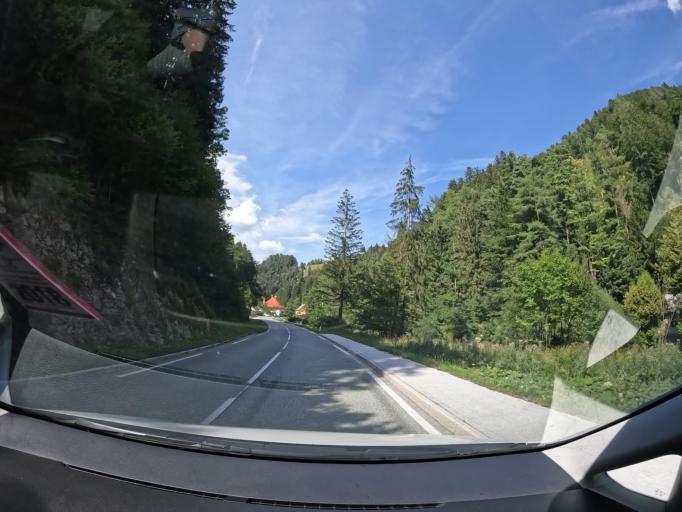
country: SI
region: Preddvor
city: Preddvor
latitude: 46.3759
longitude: 14.4000
